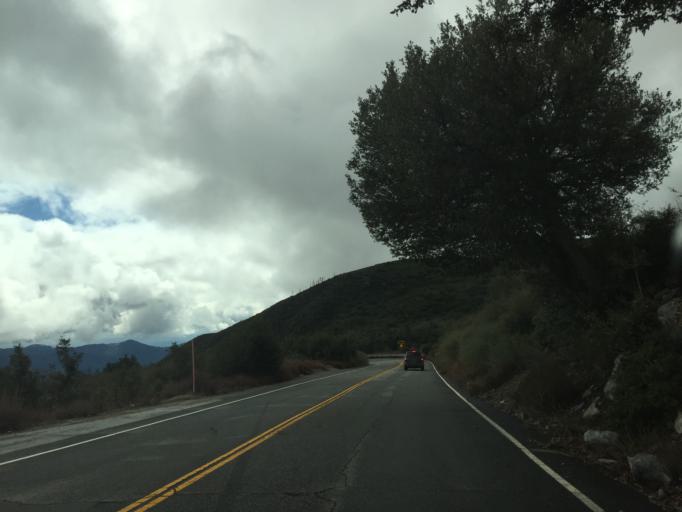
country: US
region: California
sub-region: Los Angeles County
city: Glendora
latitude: 34.3037
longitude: -117.8460
